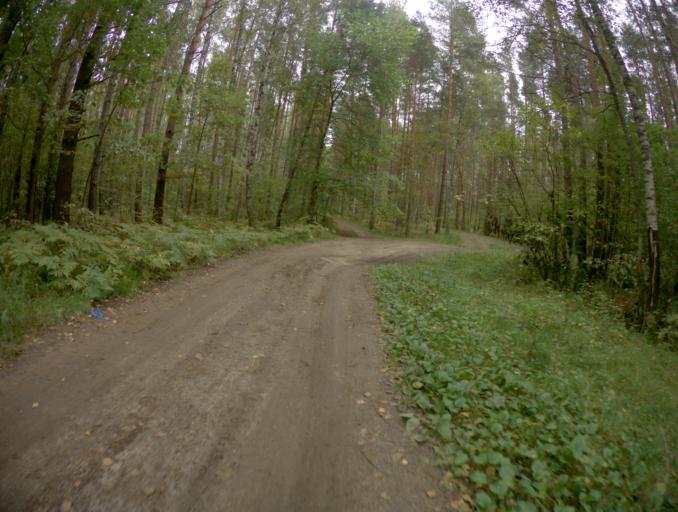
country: RU
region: Vladimir
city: Raduzhnyy
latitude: 56.0595
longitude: 40.3500
